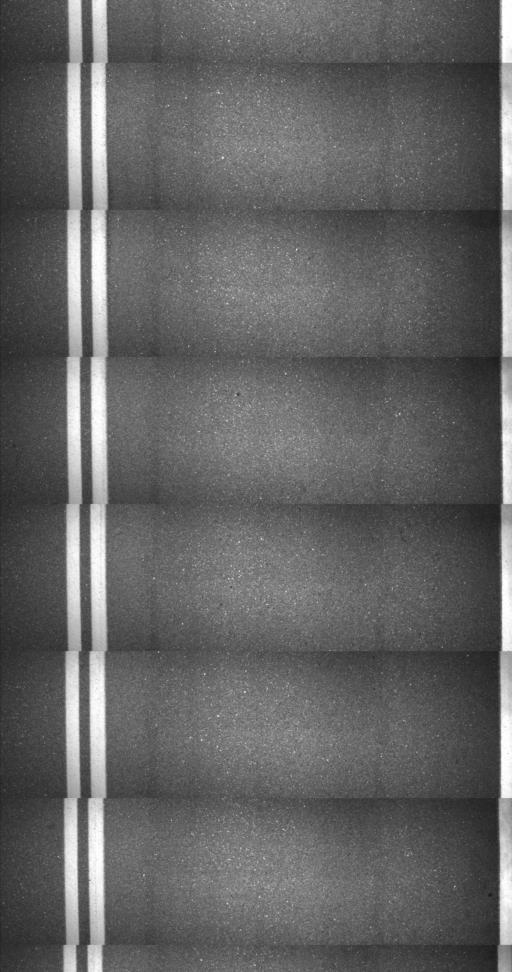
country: US
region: Massachusetts
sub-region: Berkshire County
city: North Adams
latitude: 42.8157
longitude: -73.0064
